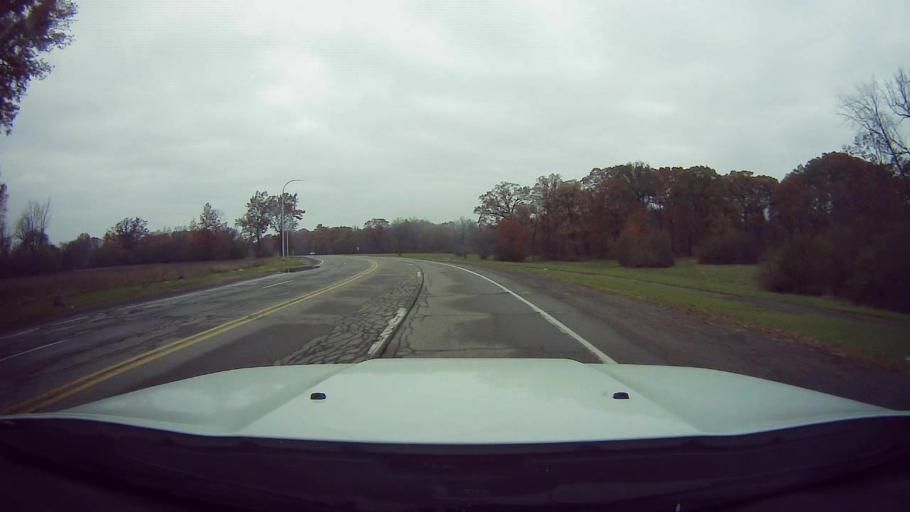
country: US
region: Michigan
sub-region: Wayne County
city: Dearborn Heights
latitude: 42.3468
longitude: -83.2502
